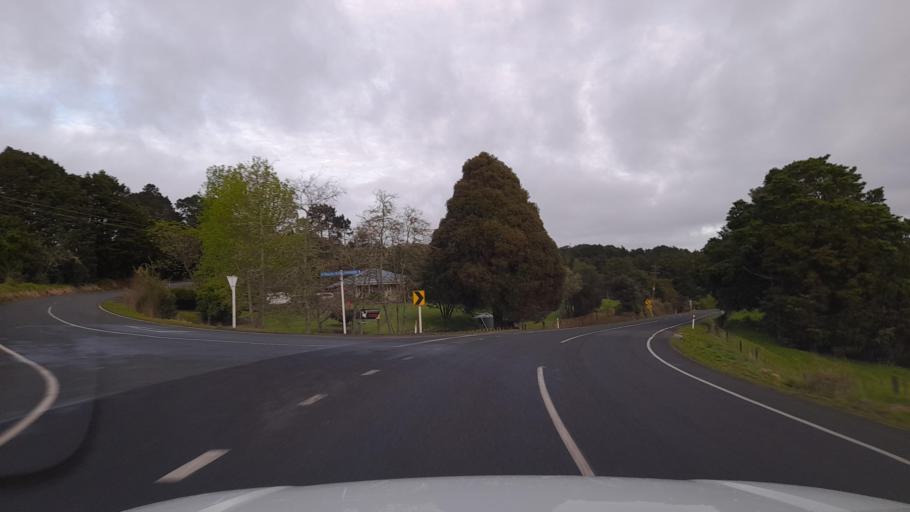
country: NZ
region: Northland
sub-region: Whangarei
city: Maungatapere
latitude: -35.7345
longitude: 174.0494
